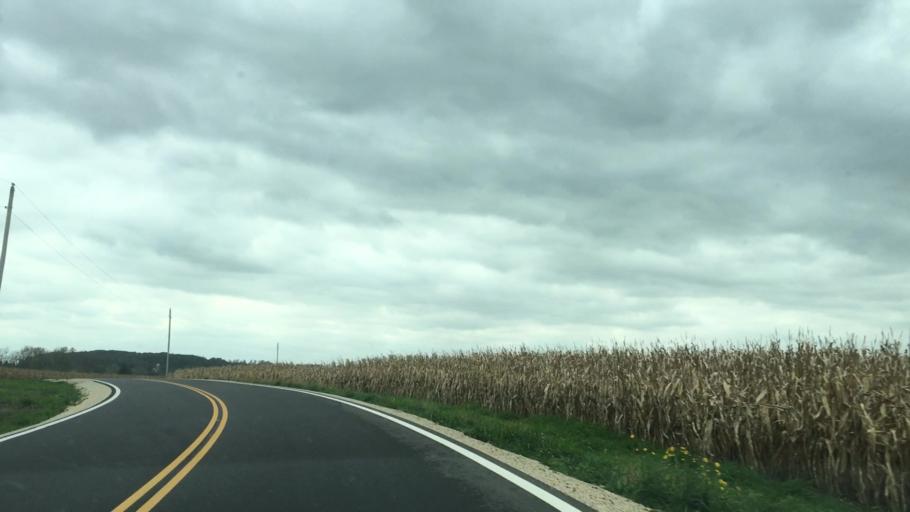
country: US
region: Minnesota
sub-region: Fillmore County
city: Preston
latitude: 43.7561
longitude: -92.0211
